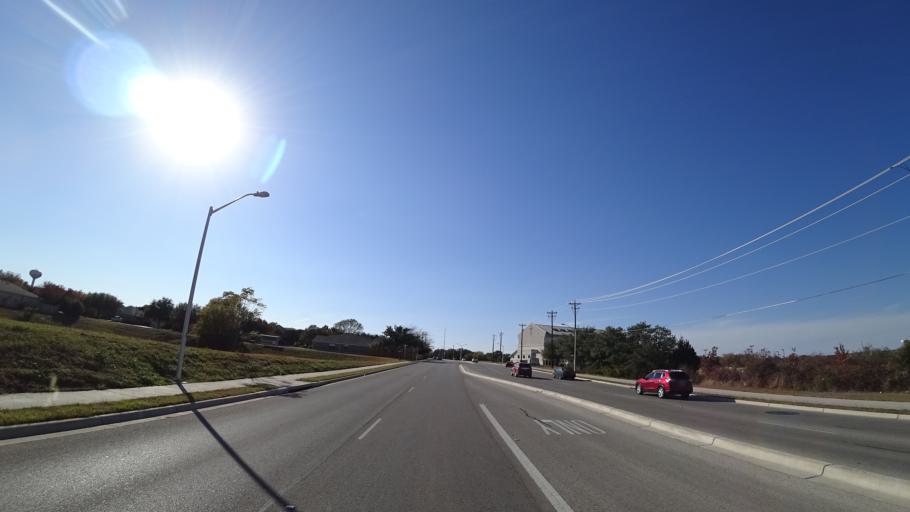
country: US
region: Texas
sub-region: Williamson County
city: Cedar Park
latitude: 30.5294
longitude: -97.8469
